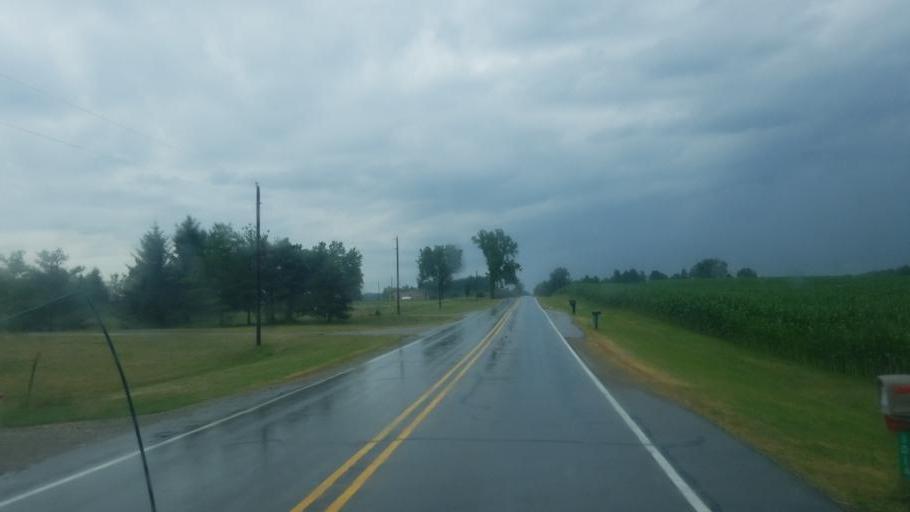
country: US
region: Indiana
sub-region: Steuben County
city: Hamilton
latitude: 41.4974
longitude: -84.8727
